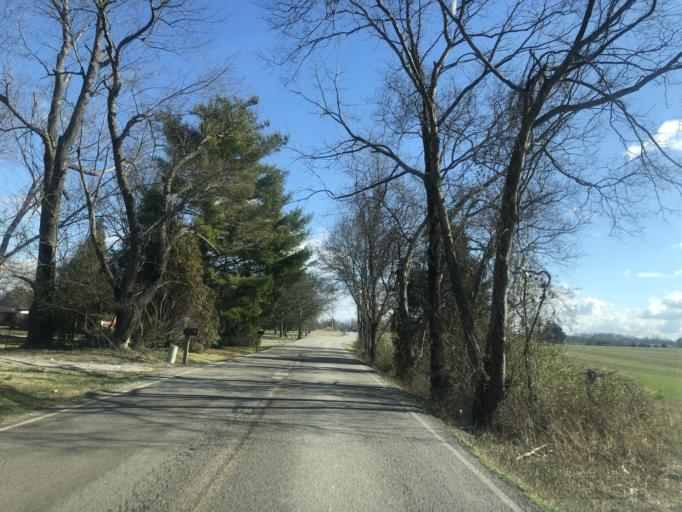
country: US
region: Tennessee
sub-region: Rutherford County
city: Smyrna
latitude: 35.8759
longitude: -86.5025
